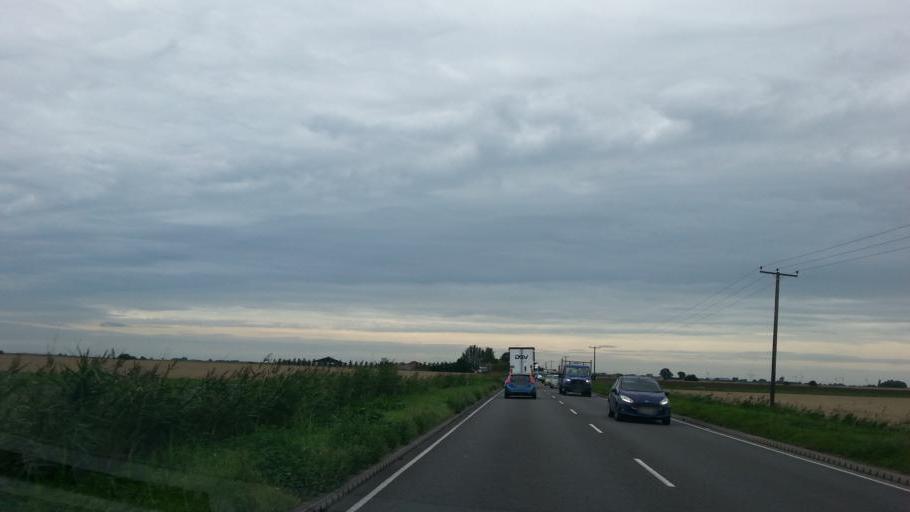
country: GB
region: England
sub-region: Cambridgeshire
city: March
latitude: 52.6086
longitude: 0.0476
